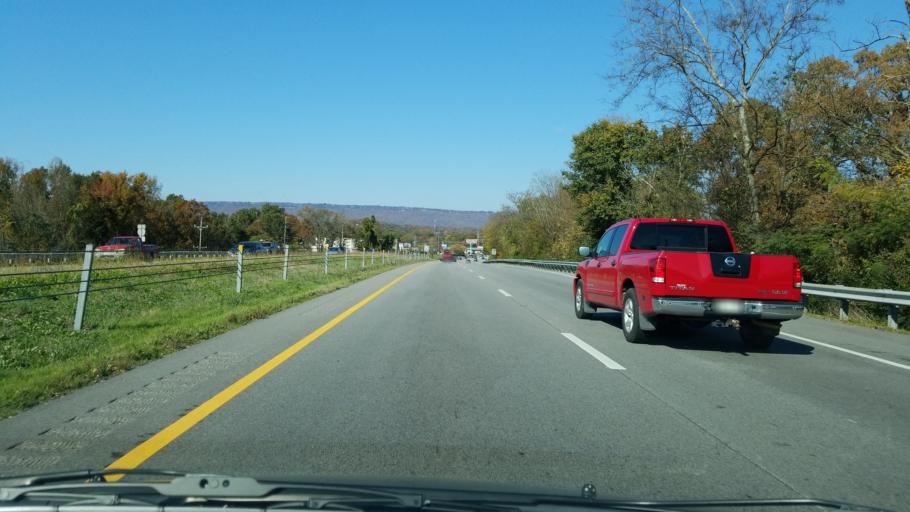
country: US
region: Tennessee
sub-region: Hamilton County
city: East Chattanooga
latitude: 35.1180
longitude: -85.2345
